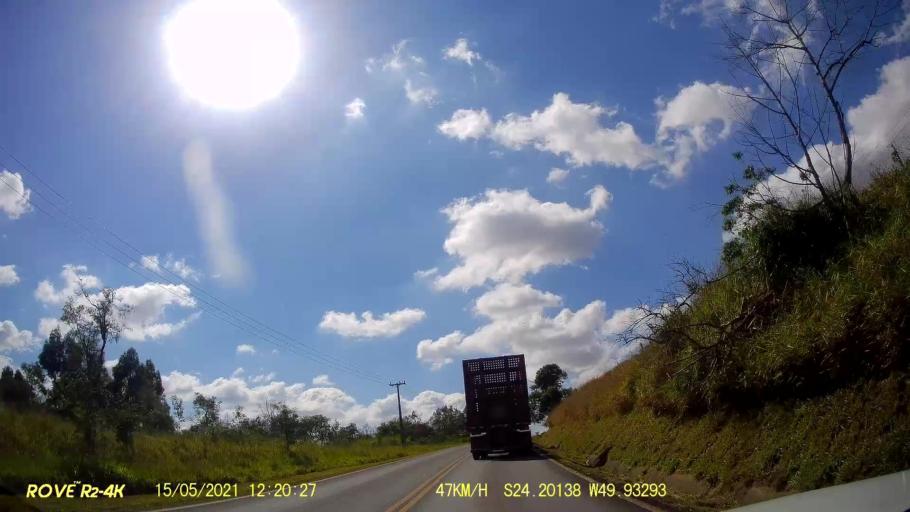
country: BR
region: Parana
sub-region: Jaguariaiva
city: Jaguariaiva
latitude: -24.2015
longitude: -49.9329
